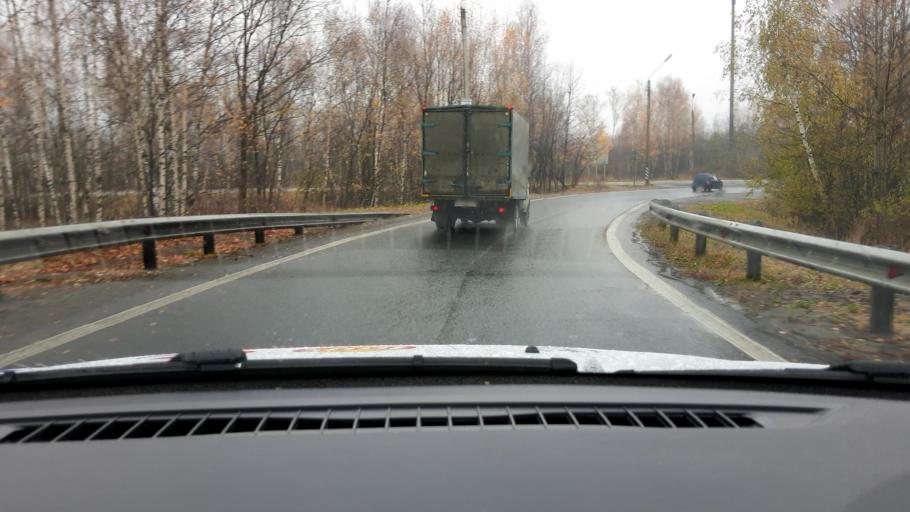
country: RU
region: Nizjnij Novgorod
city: Gorbatovka
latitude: 56.2636
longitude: 43.7097
